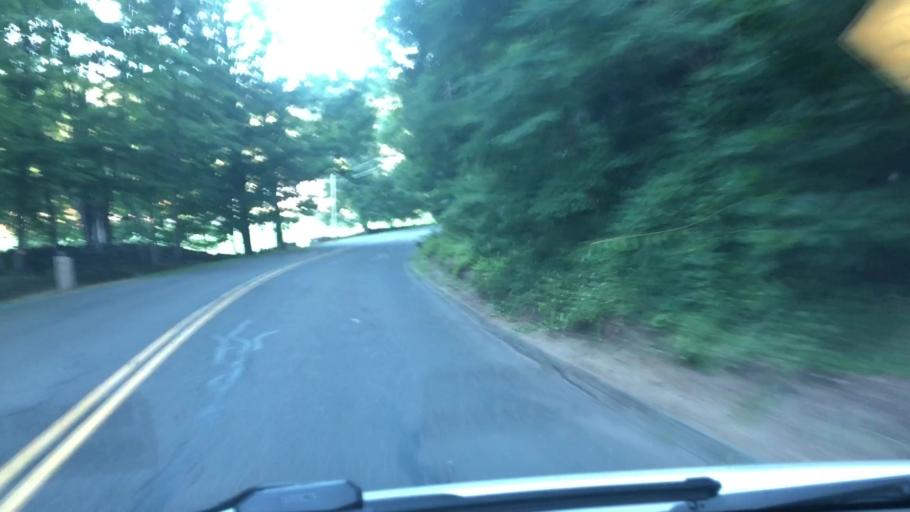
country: US
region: Massachusetts
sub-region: Hampshire County
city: Williamsburg
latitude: 42.3696
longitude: -72.7302
